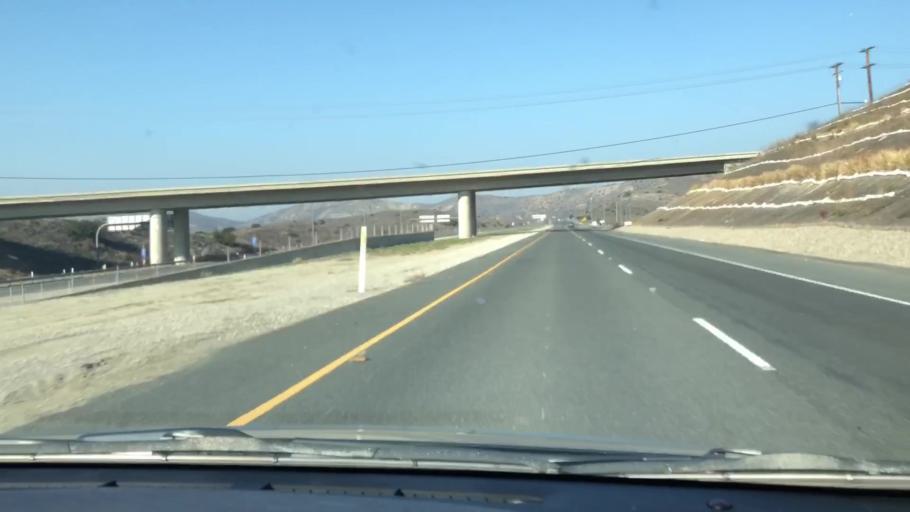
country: US
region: California
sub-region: Orange County
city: Foothill Ranch
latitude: 33.7168
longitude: -117.7201
